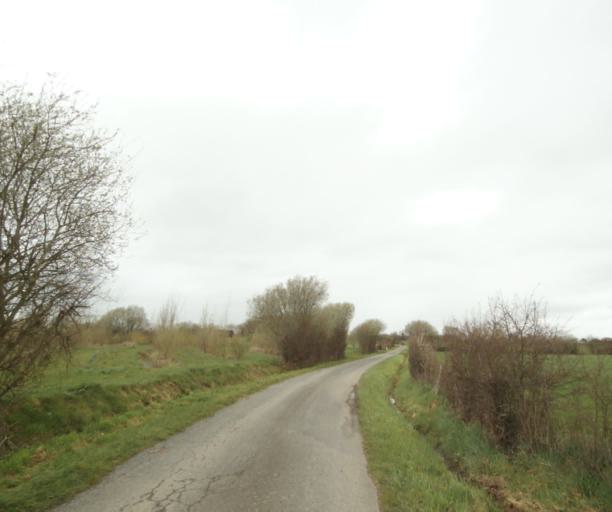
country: FR
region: Pays de la Loire
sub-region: Departement de la Loire-Atlantique
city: Bouvron
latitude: 47.4287
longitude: -1.8465
